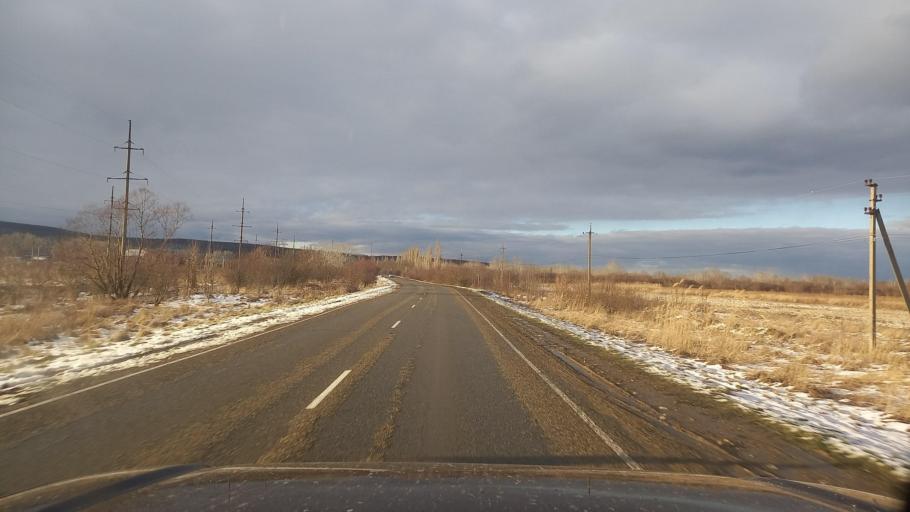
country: RU
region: Krasnodarskiy
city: Smolenskaya
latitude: 44.7747
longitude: 38.8157
